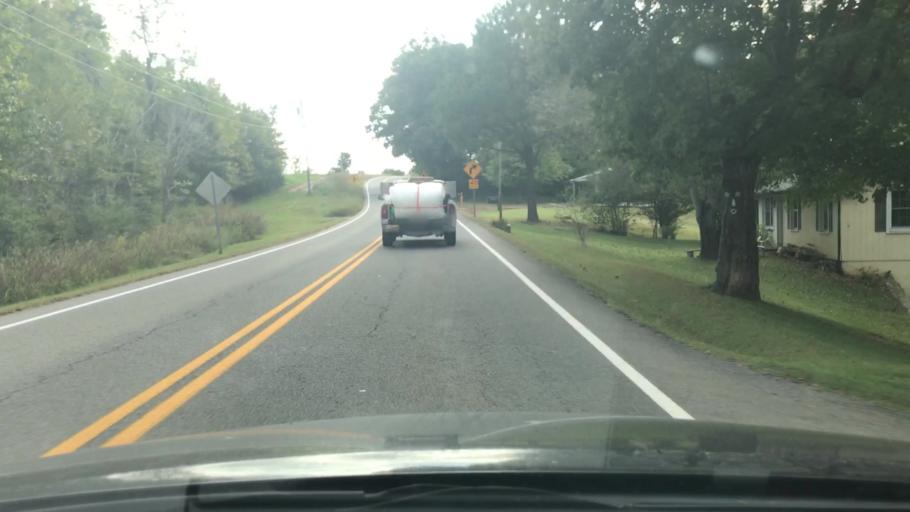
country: US
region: Tennessee
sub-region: Cheatham County
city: Ashland City
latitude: 36.2773
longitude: -87.1868
